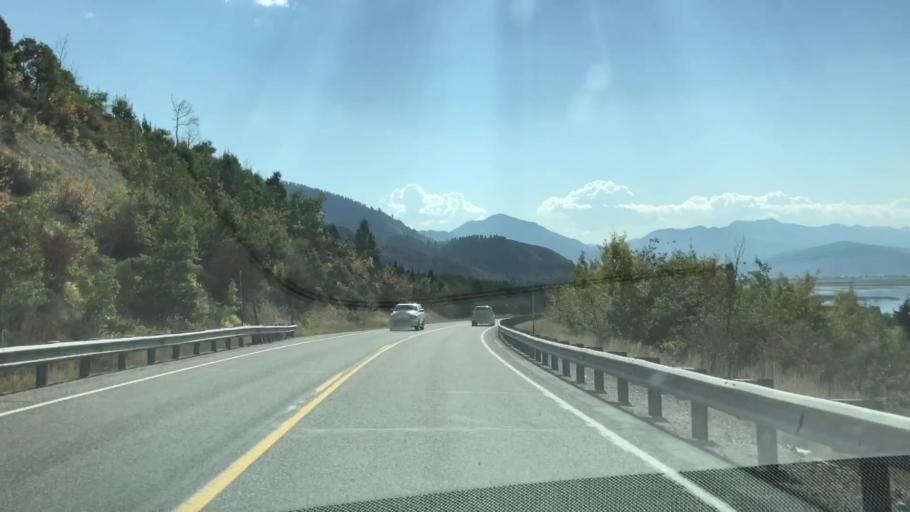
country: US
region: Wyoming
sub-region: Teton County
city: Hoback
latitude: 43.2256
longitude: -111.0793
